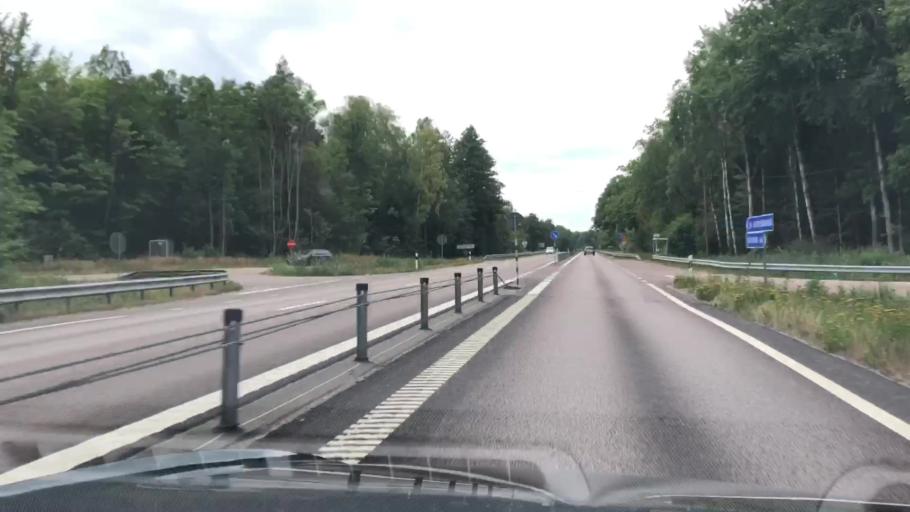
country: SE
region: Blekinge
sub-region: Karlskrona Kommun
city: Jaemjoe
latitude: 56.2322
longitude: 15.9175
